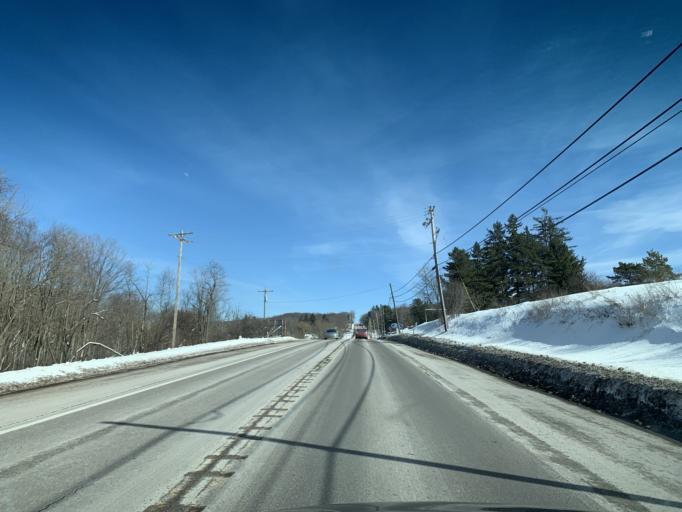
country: US
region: Pennsylvania
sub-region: Somerset County
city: Meyersdale
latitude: 39.6955
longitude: -79.1183
